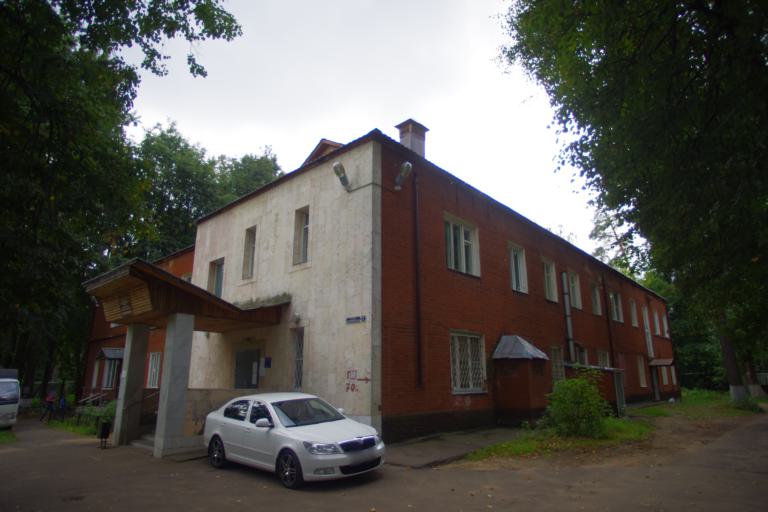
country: RU
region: Moskovskaya
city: Krasnogorsk
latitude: 55.8301
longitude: 37.3305
